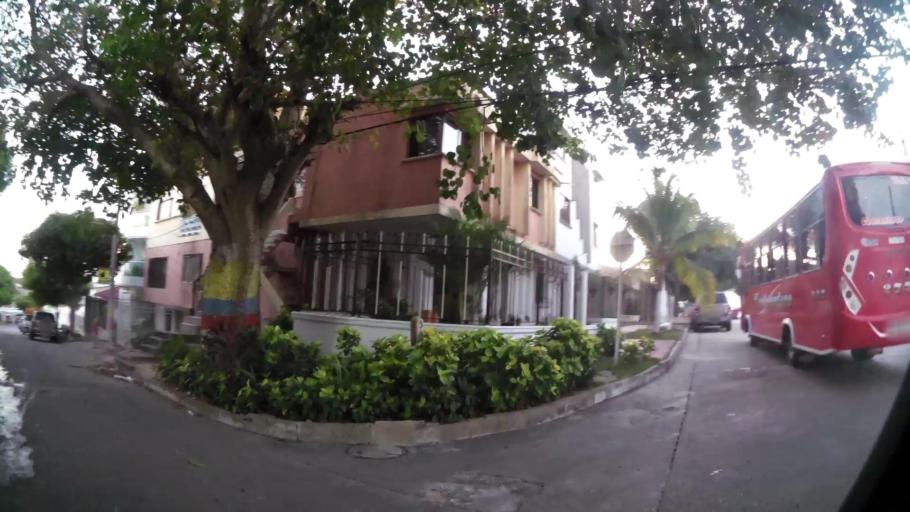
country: CO
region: Atlantico
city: Barranquilla
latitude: 10.9829
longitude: -74.8074
